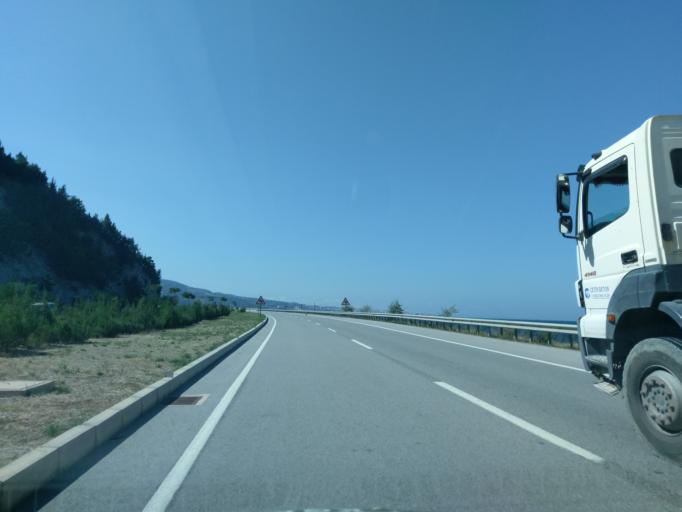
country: TR
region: Sinop
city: Gerze
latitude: 41.7491
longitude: 35.2410
